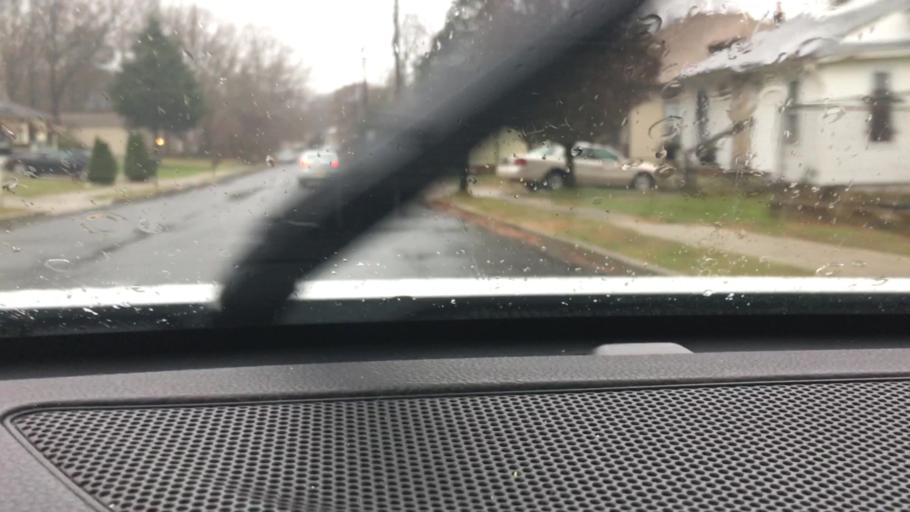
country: US
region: New Jersey
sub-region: Atlantic County
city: Pleasantville
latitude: 39.4031
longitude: -74.5301
